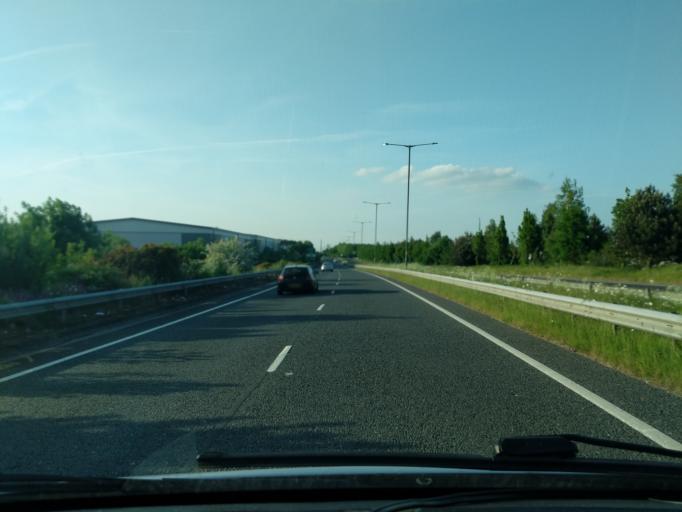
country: GB
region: England
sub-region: St. Helens
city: St Helens
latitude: 53.4242
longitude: -2.7406
